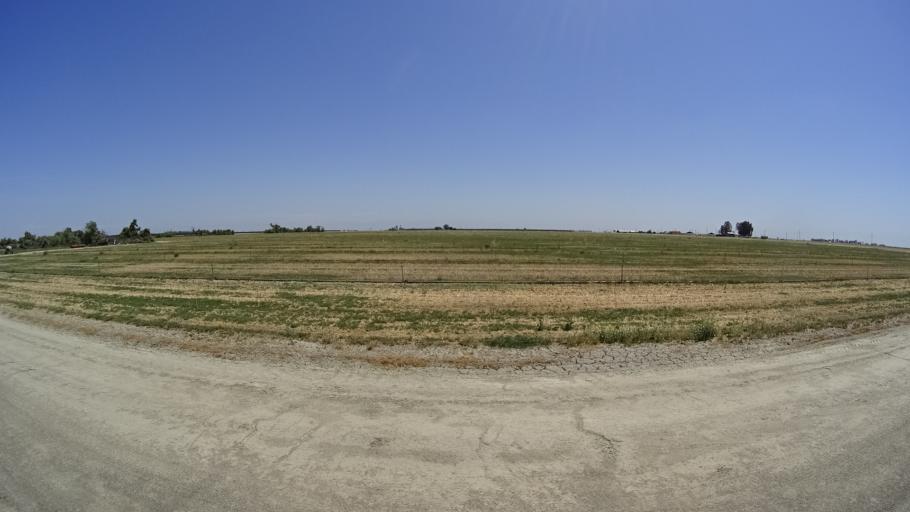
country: US
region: California
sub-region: Kings County
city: Armona
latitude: 36.2297
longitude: -119.7266
